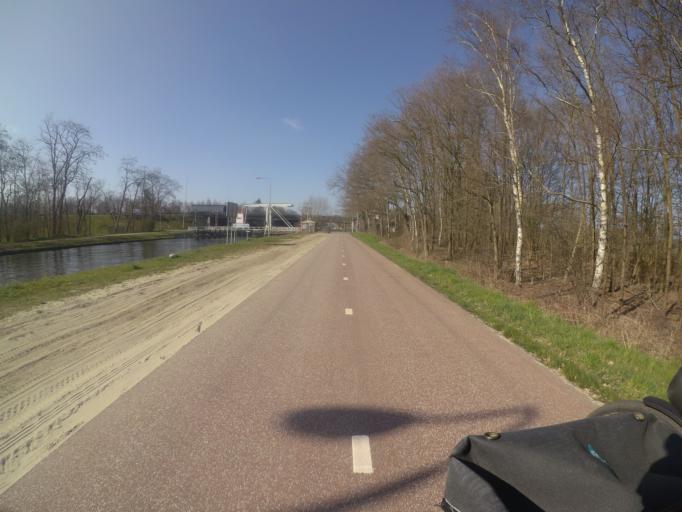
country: NL
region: North Brabant
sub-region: Gemeente Tilburg
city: Tilburg
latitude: 51.5454
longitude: 5.1194
